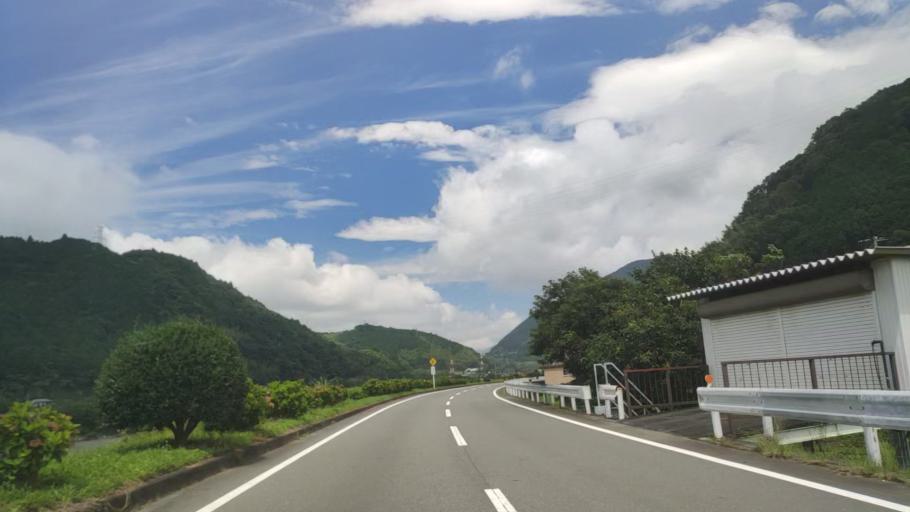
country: JP
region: Shizuoka
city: Fujinomiya
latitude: 35.2301
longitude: 138.5131
